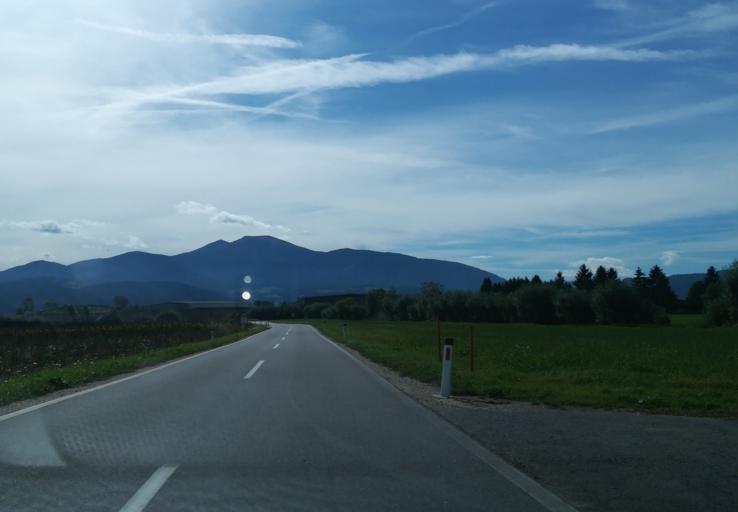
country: AT
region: Styria
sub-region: Politischer Bezirk Murtal
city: Flatschach
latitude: 47.2098
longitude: 14.7567
